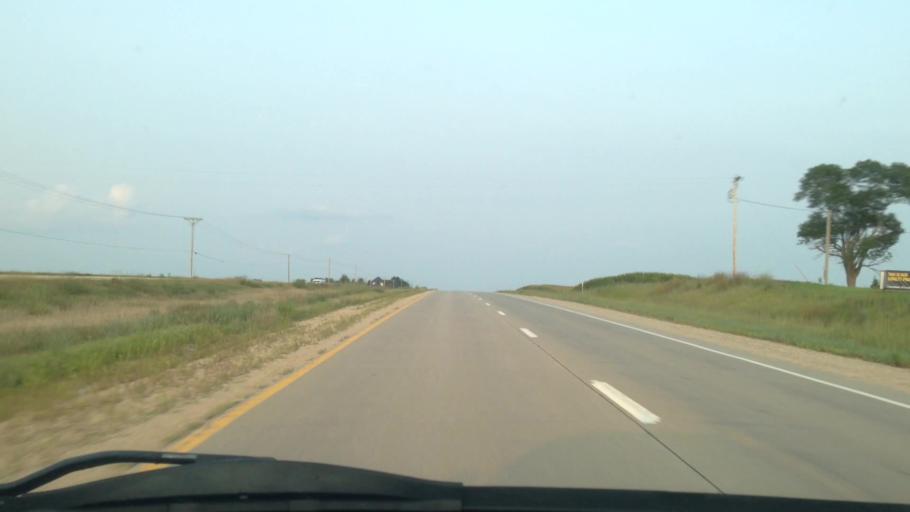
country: US
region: Iowa
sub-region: Benton County
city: Atkins
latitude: 41.9632
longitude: -91.9587
